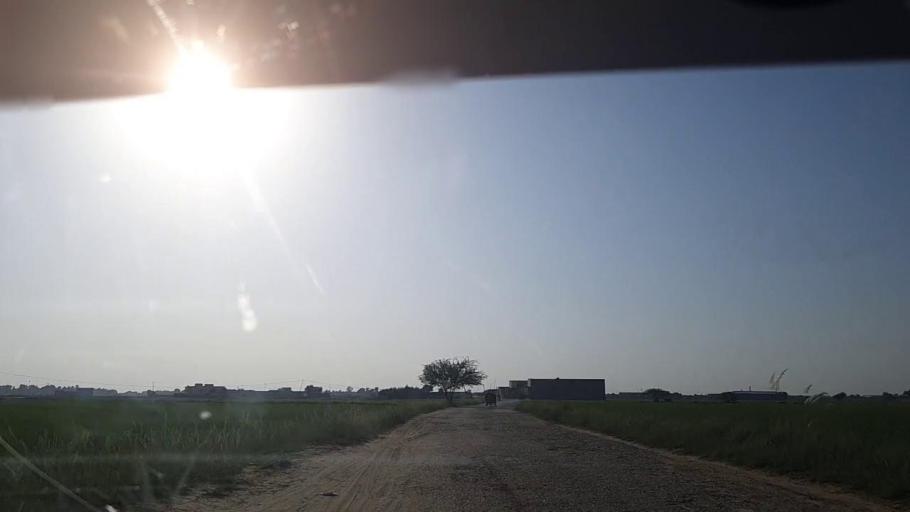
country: PK
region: Sindh
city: Tangwani
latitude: 28.2607
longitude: 69.0094
